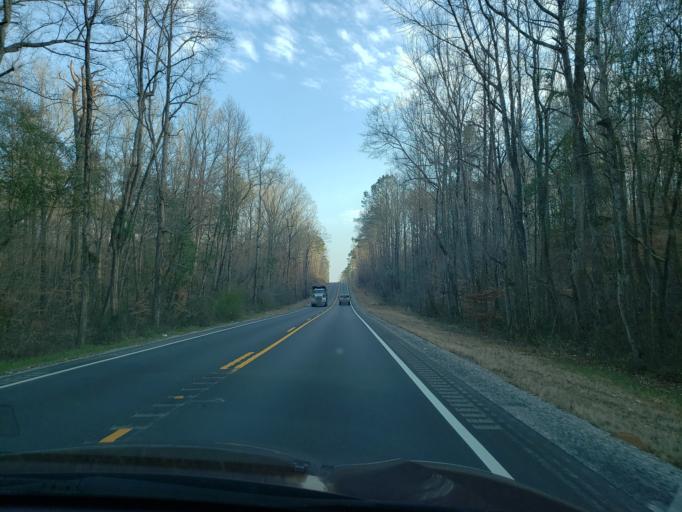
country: US
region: Alabama
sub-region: Hale County
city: Greensboro
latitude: 32.8431
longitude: -87.6093
